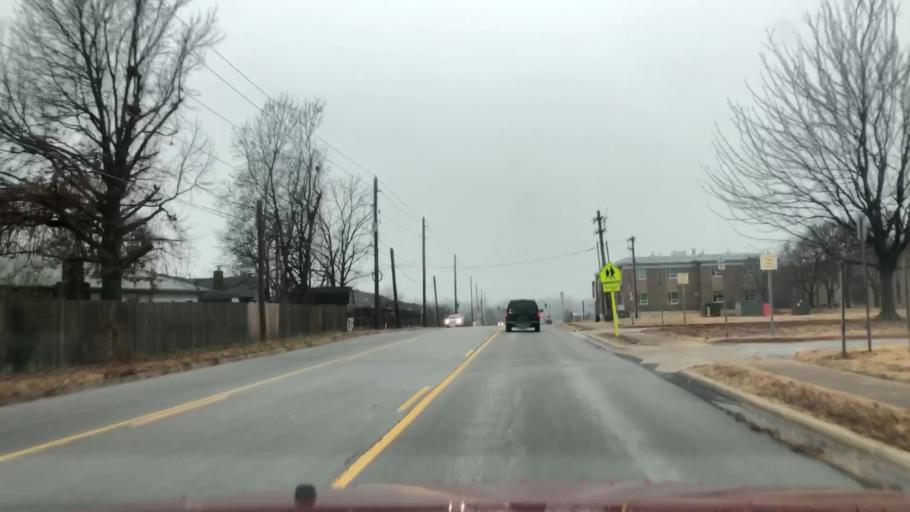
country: US
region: Missouri
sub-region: Greene County
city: Springfield
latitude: 37.1455
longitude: -93.2887
